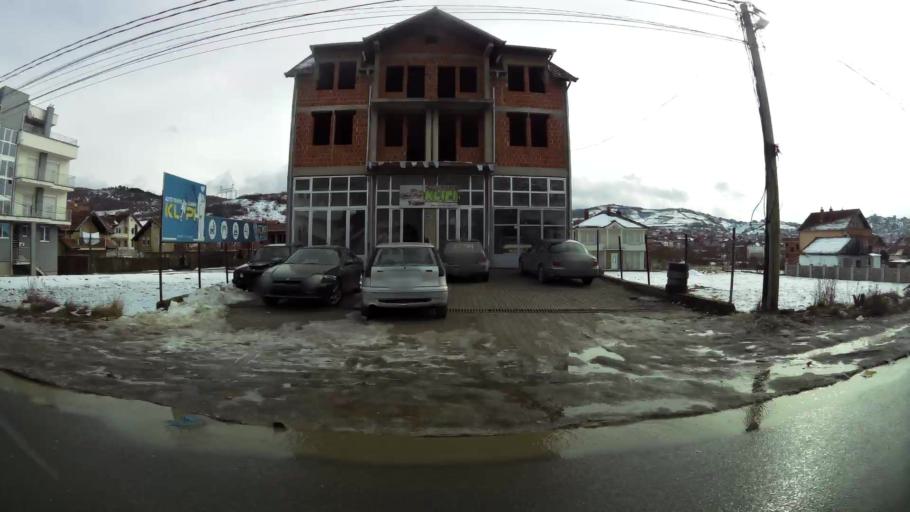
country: XK
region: Pristina
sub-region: Komuna e Prishtines
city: Pristina
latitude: 42.6887
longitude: 21.1781
